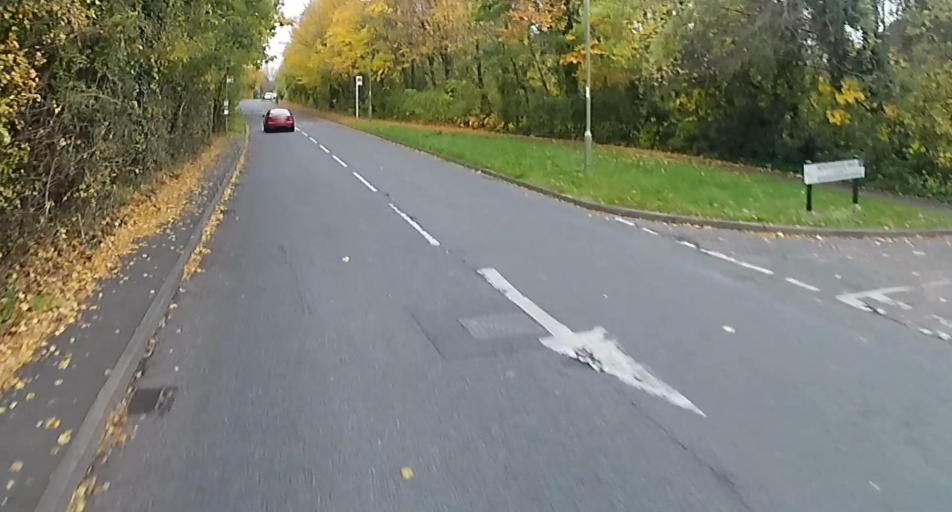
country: GB
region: England
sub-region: Hampshire
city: Basingstoke
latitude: 51.2347
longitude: -1.1378
